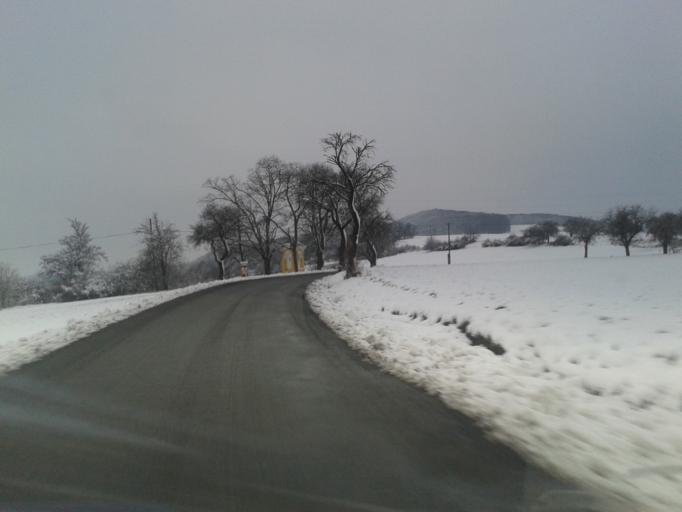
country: CZ
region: Central Bohemia
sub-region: Okres Beroun
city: Lodenice
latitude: 49.9133
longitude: 14.1423
